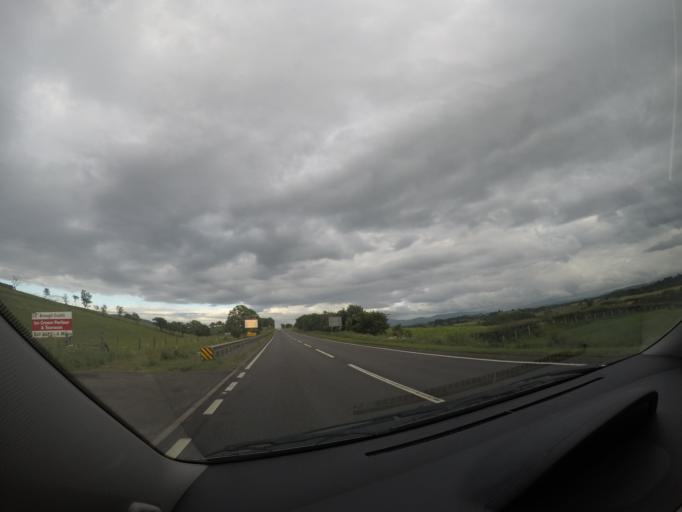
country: GB
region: England
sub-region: Cumbria
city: Appleby-in-Westmorland
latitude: 54.5527
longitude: -2.4258
